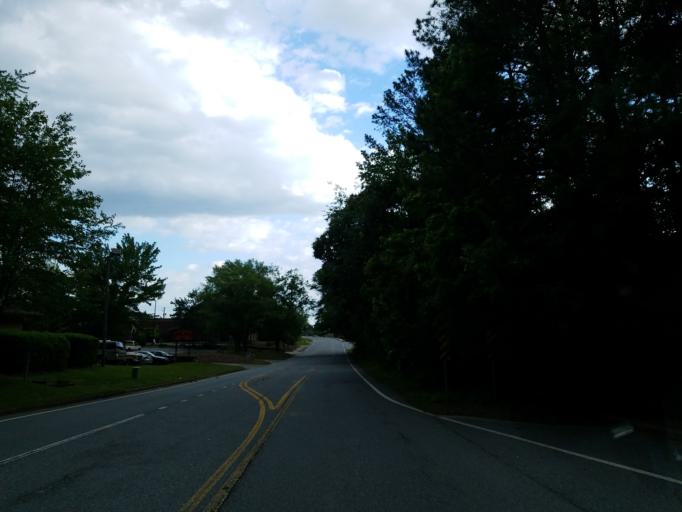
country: US
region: Georgia
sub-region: Fulton County
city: Roswell
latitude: 34.0414
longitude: -84.3437
